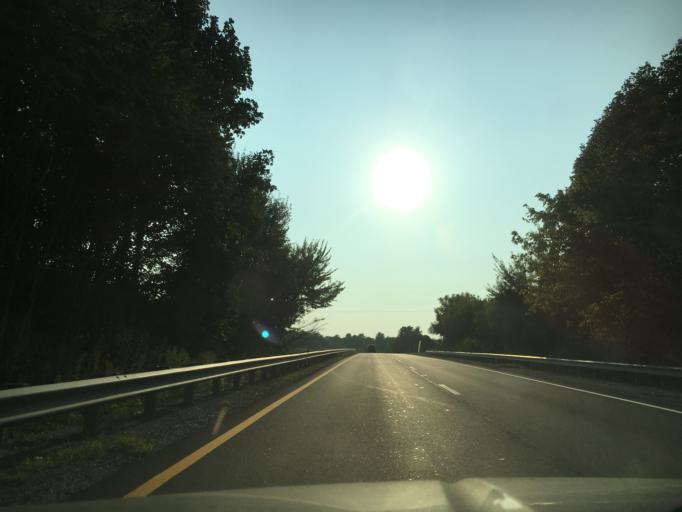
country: US
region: Virginia
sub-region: Prince Edward County
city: Hampden Sydney
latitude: 37.3033
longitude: -78.5444
